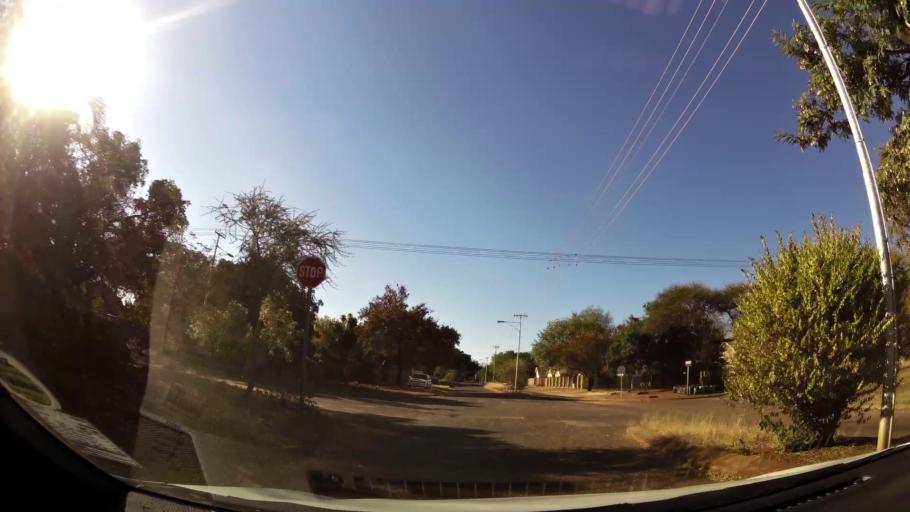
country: ZA
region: Limpopo
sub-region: Waterberg District Municipality
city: Mokopane
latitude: -24.2083
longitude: 29.0071
